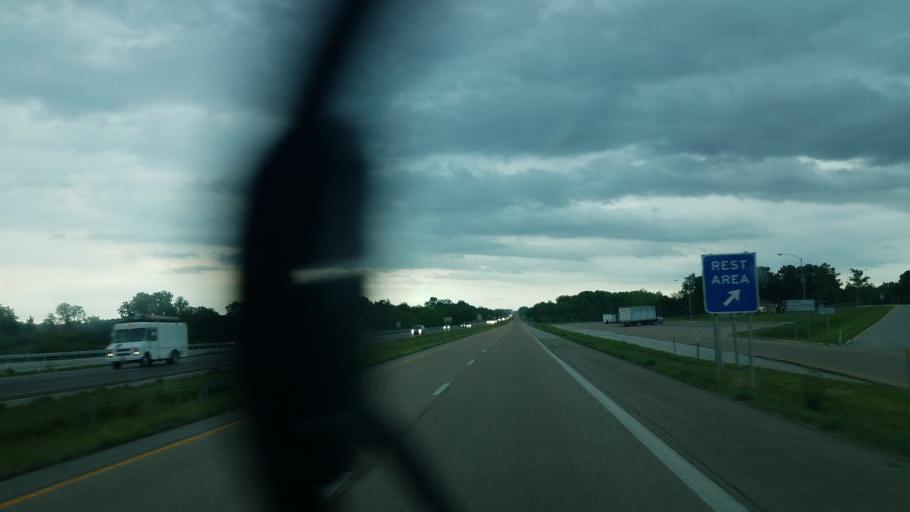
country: US
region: Missouri
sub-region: Cooper County
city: Boonville
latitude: 38.9366
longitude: -92.7290
